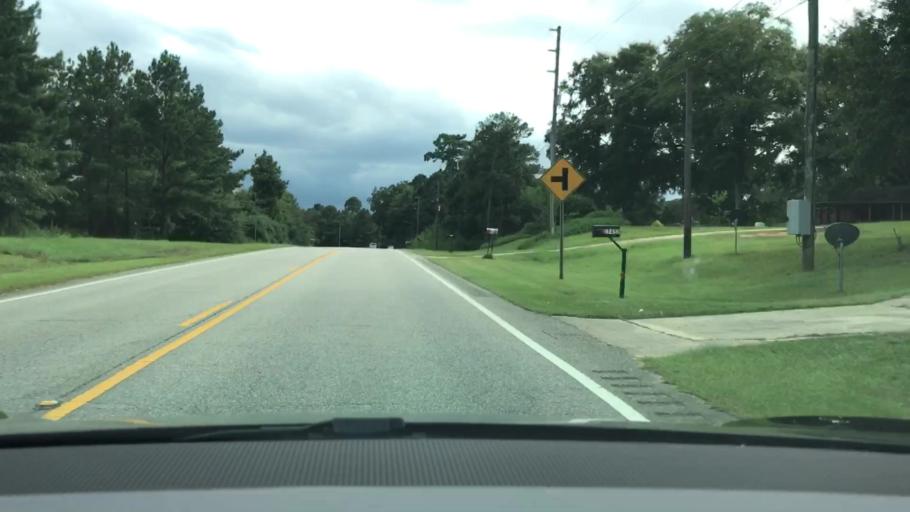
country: US
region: Alabama
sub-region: Coffee County
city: Elba
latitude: 31.5433
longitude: -86.0221
